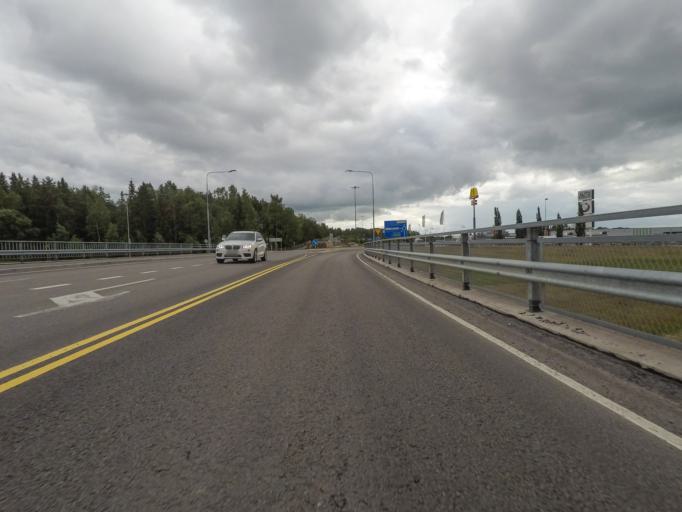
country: FI
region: Varsinais-Suomi
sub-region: Turku
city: Raisio
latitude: 60.4907
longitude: 22.1895
